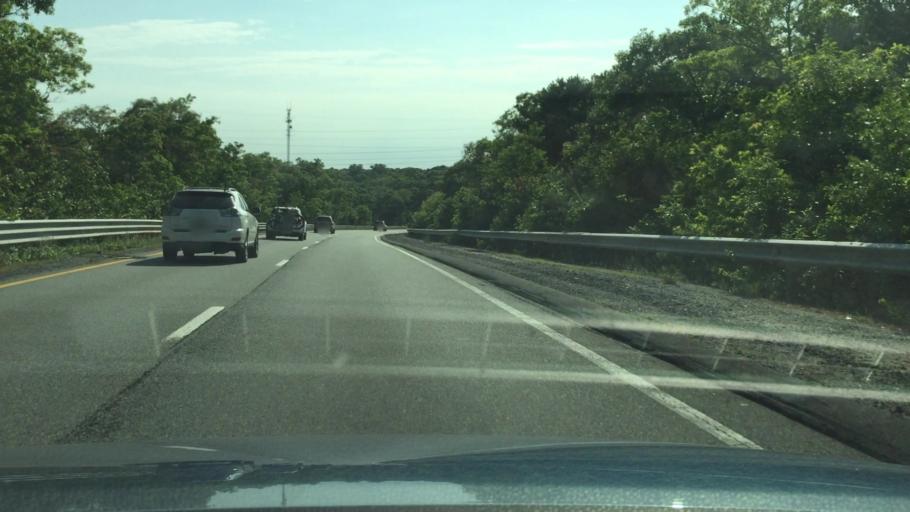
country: US
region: Massachusetts
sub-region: Barnstable County
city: West Barnstable
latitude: 41.6854
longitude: -70.3478
